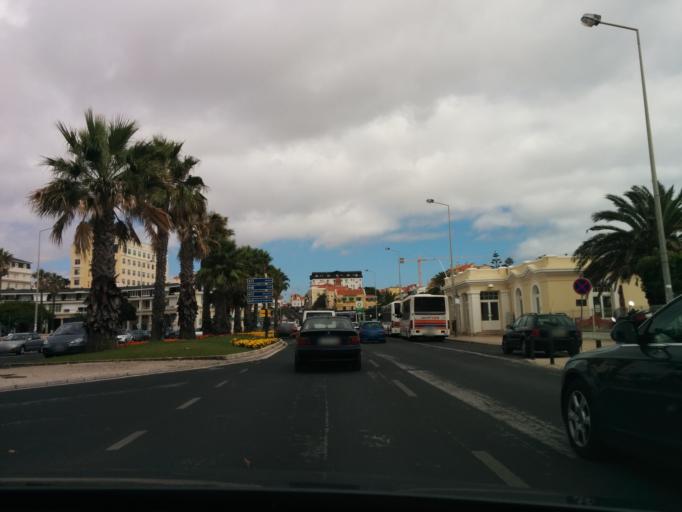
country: PT
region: Lisbon
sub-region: Cascais
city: Estoril
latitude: 38.7036
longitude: -9.3993
